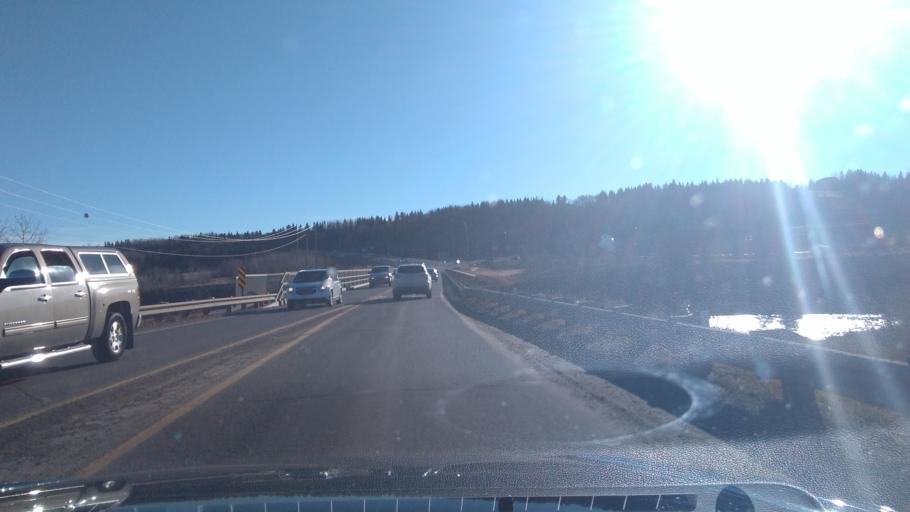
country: CA
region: Alberta
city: Cochrane
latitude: 51.1839
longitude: -114.4867
